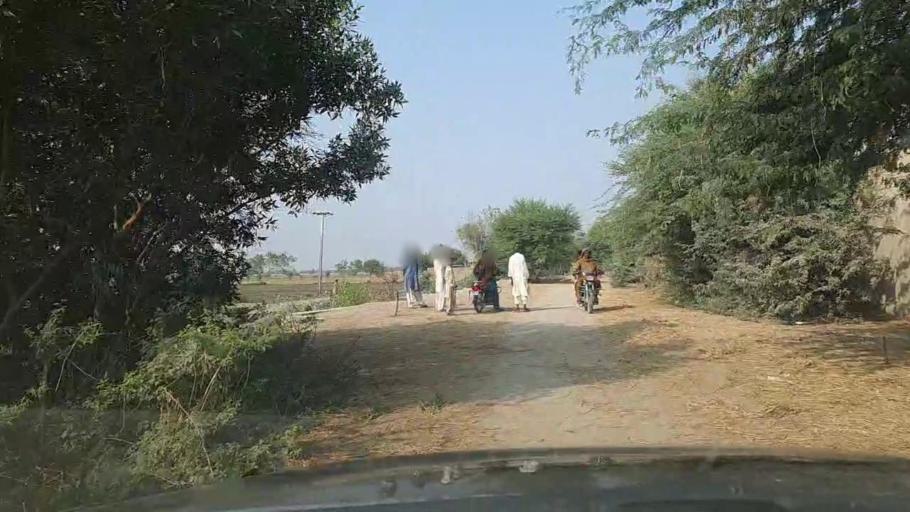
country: PK
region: Sindh
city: Mirpur Batoro
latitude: 24.7084
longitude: 68.2542
